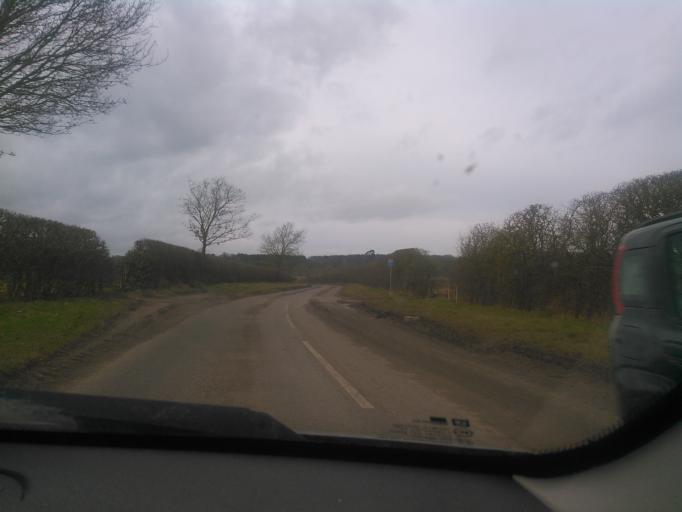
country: GB
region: England
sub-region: Shropshire
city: Shawbury
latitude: 52.8153
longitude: -2.6644
